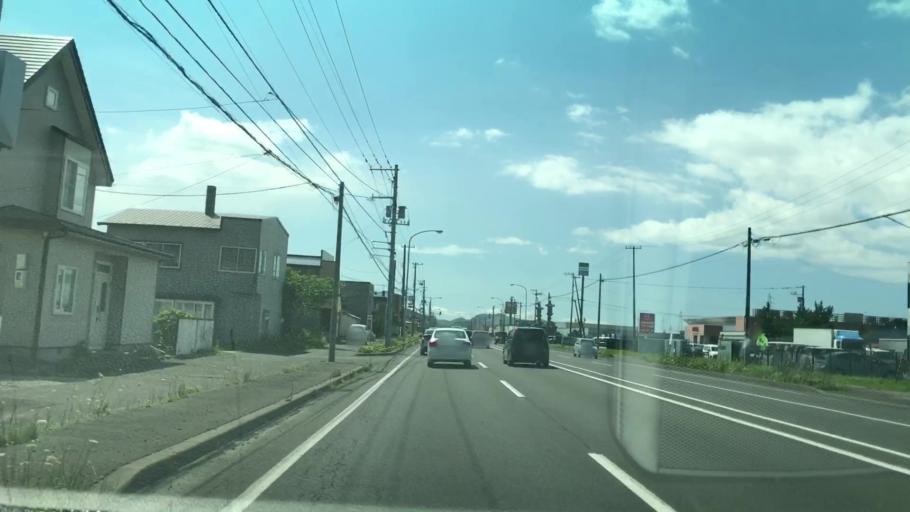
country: JP
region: Hokkaido
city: Muroran
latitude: 42.3730
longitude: 141.0659
